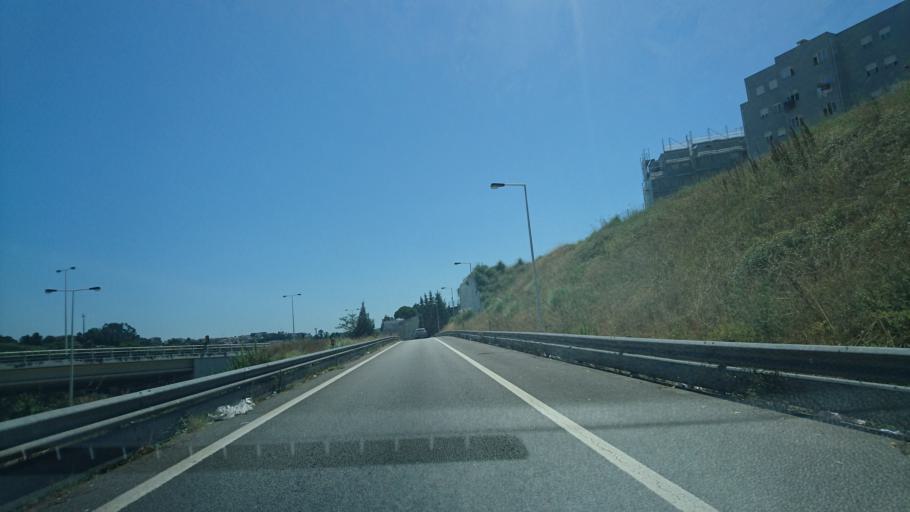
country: PT
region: Porto
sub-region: Gondomar
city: Valbom
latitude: 41.1571
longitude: -8.5724
